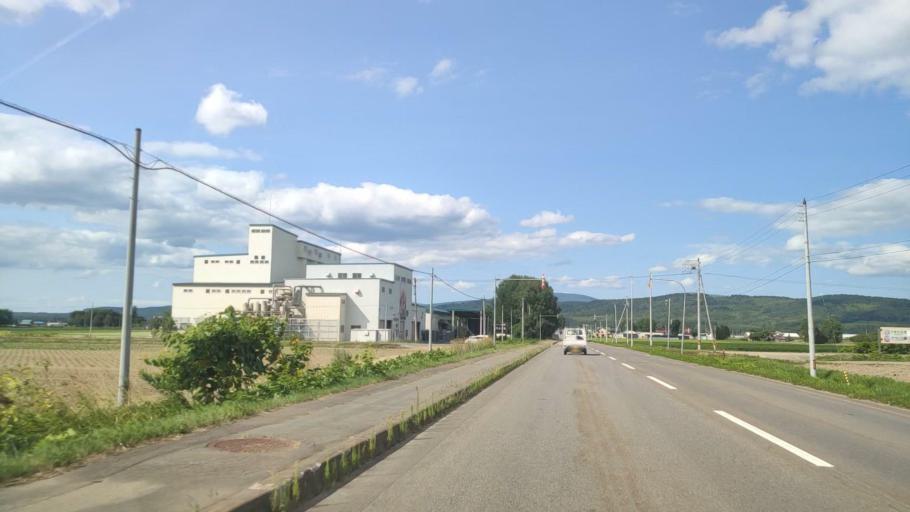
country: JP
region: Hokkaido
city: Nayoro
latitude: 44.4315
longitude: 142.4011
